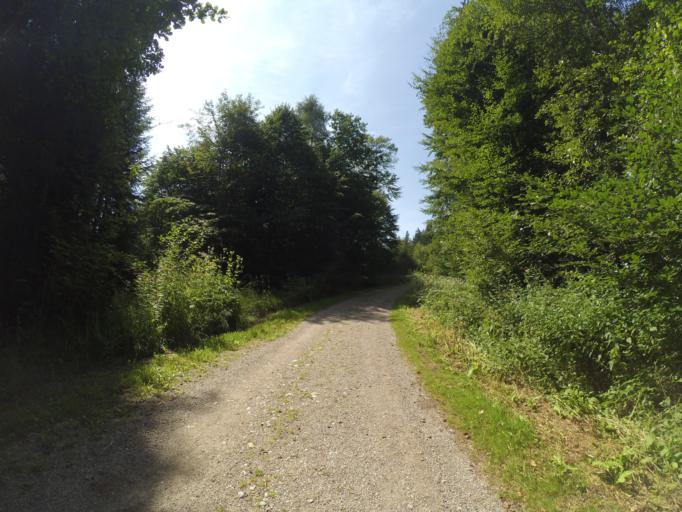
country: DE
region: Bavaria
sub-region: Swabia
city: Bad Worishofen
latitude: 47.9933
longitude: 10.5656
